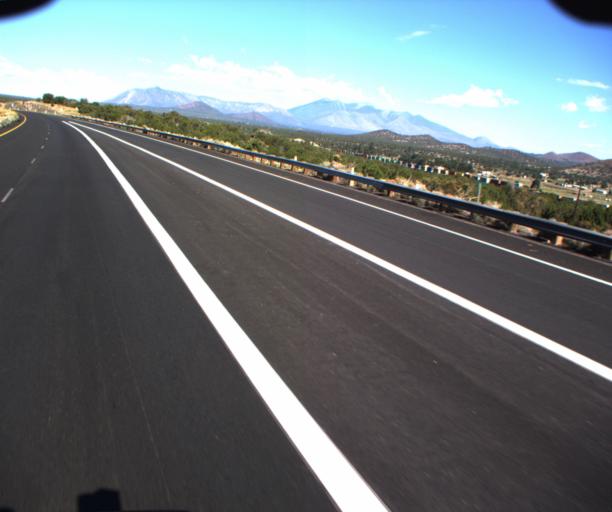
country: US
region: Arizona
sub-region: Coconino County
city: Flagstaff
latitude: 35.2029
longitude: -111.4116
